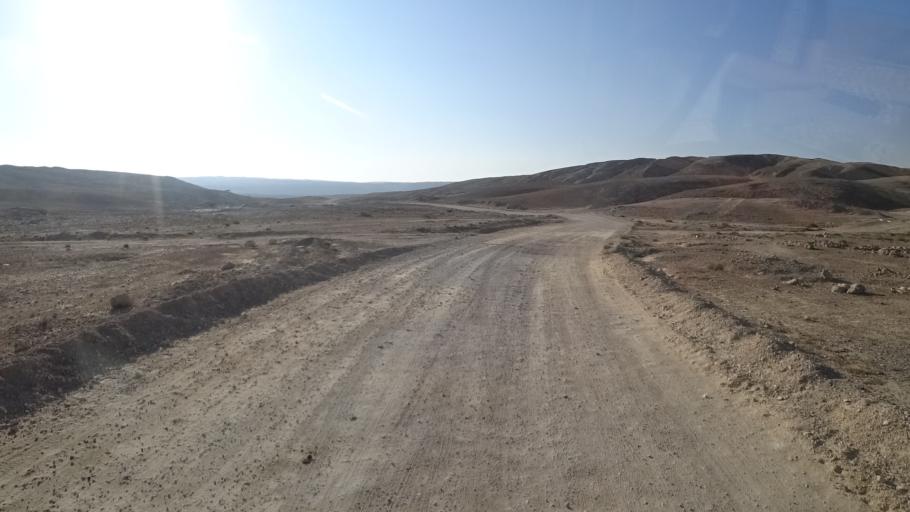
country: OM
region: Zufar
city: Salalah
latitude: 17.2421
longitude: 53.9140
